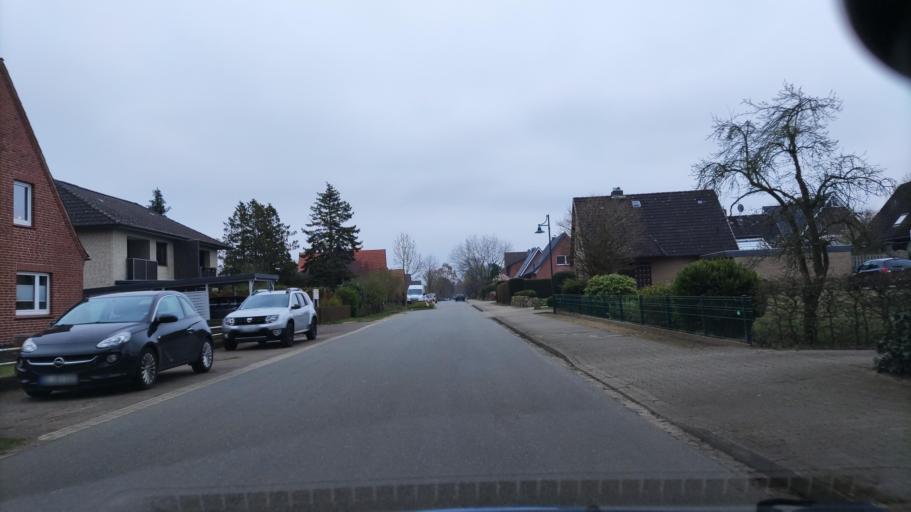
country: DE
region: Lower Saxony
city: Wulfsen
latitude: 53.3027
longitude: 10.1379
